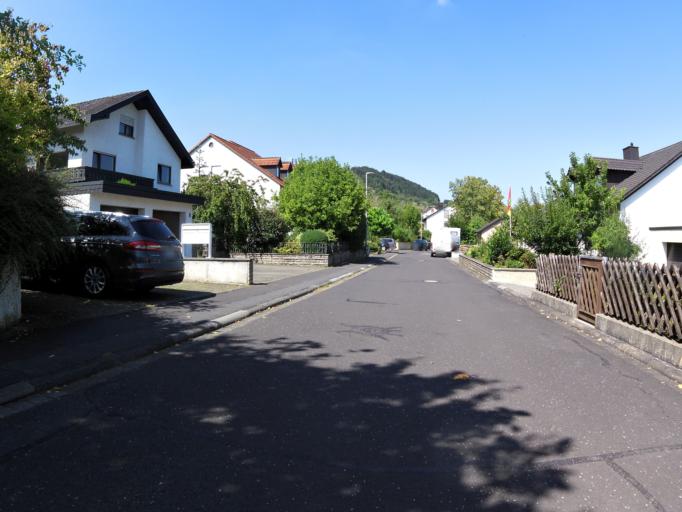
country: DE
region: Bavaria
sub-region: Regierungsbezirk Unterfranken
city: Erlabrunn
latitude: 49.8566
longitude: 9.8441
